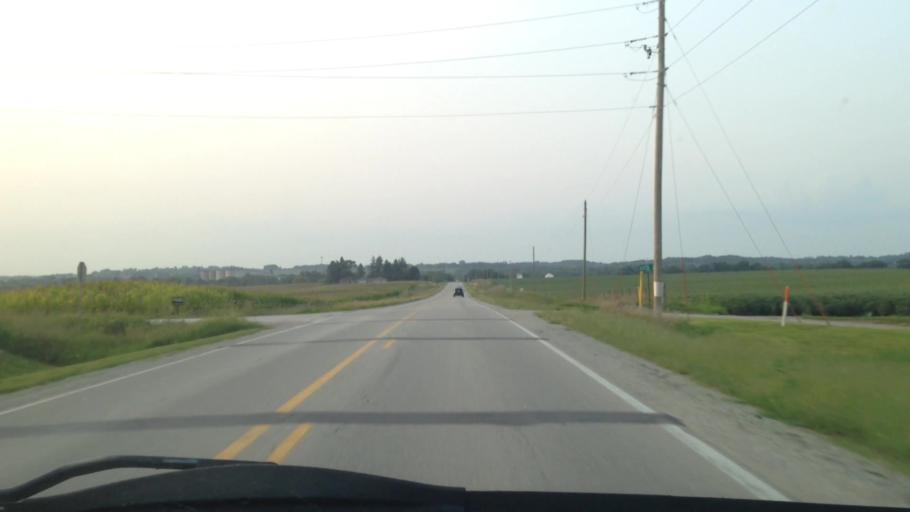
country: US
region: Iowa
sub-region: Linn County
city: Palo
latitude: 42.0797
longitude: -91.8690
